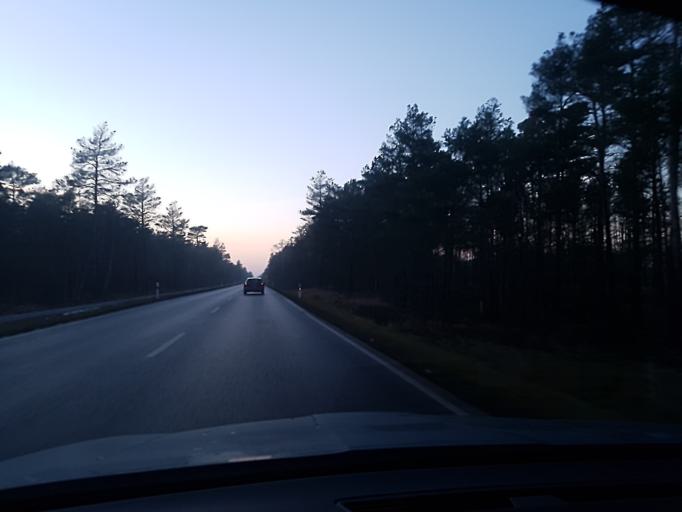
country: DE
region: Brandenburg
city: Finsterwalde
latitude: 51.6335
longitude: 13.6555
